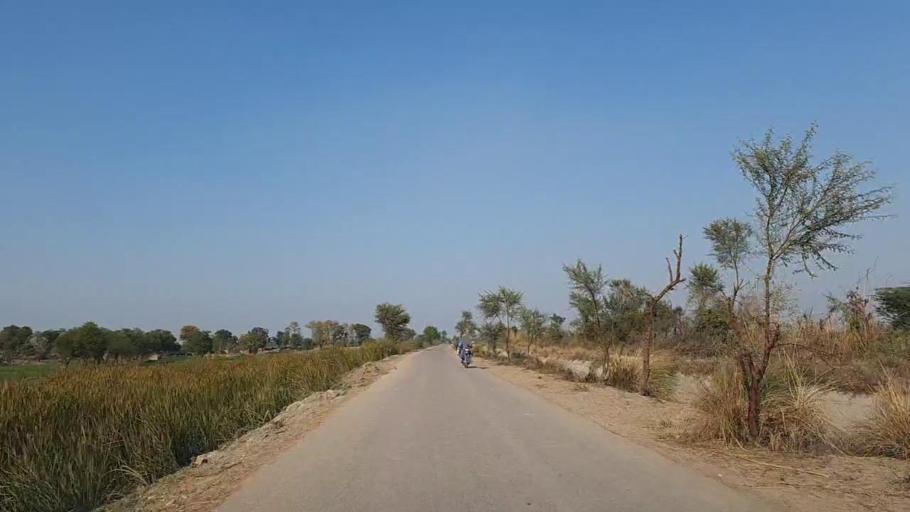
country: PK
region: Sindh
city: Daur
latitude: 26.4196
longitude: 68.2601
